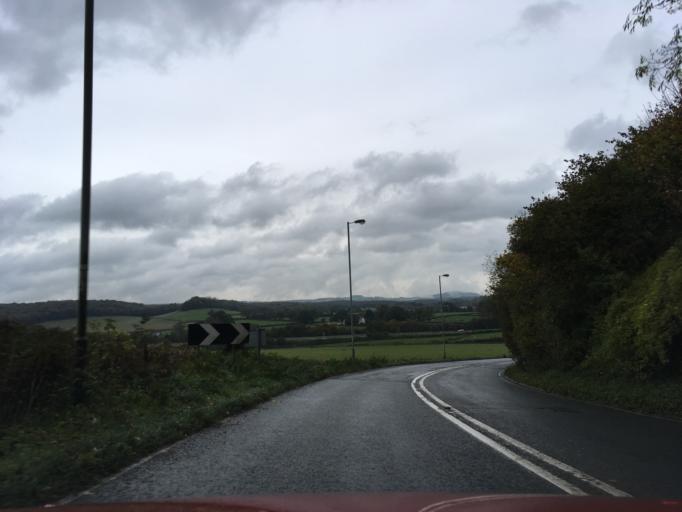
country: GB
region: Wales
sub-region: Monmouthshire
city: Chepstow
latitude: 51.6138
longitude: -2.7139
